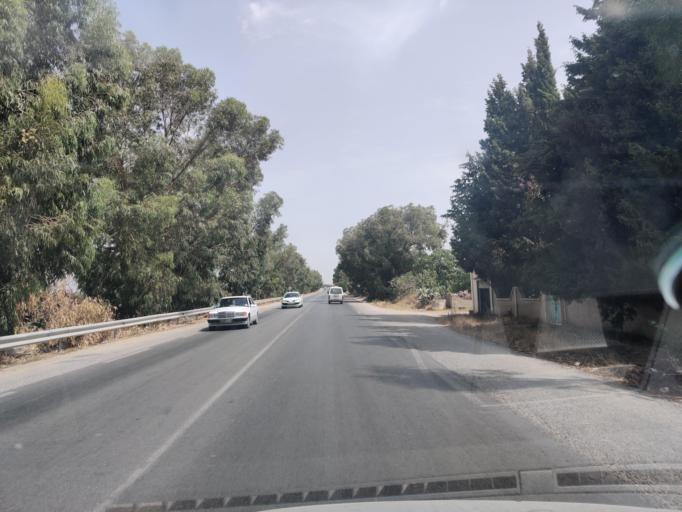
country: TN
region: Nabul
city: Al Hammamat
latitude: 36.4611
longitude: 10.5707
